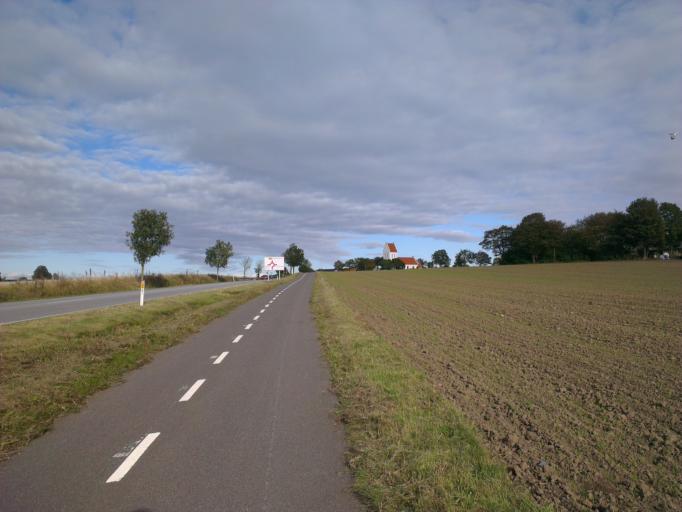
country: DK
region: Zealand
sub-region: Lejre Kommune
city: Ejby
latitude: 55.7016
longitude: 11.8836
